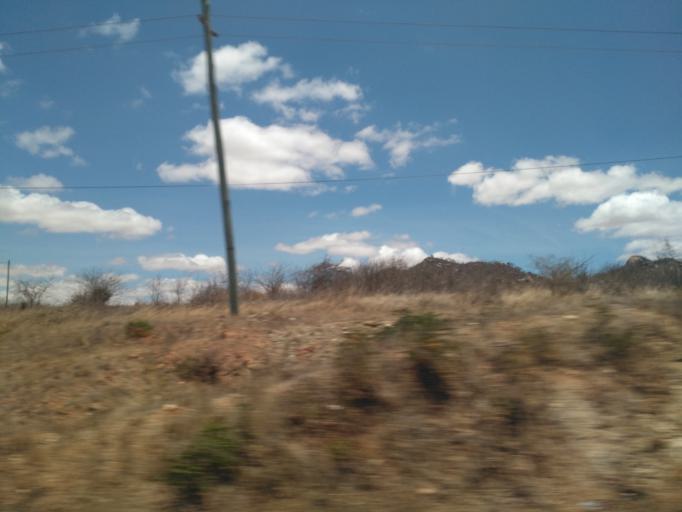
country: TZ
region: Dodoma
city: Kisasa
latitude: -6.2202
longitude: 35.8101
